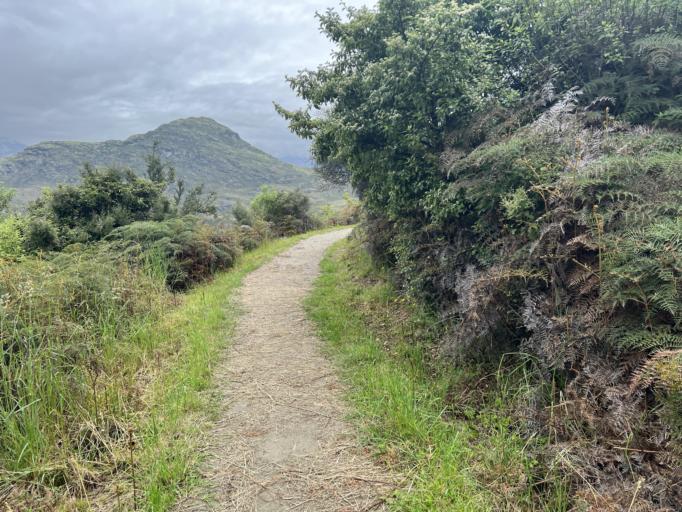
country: NZ
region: Otago
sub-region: Queenstown-Lakes District
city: Wanaka
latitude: -44.6452
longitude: 168.9678
